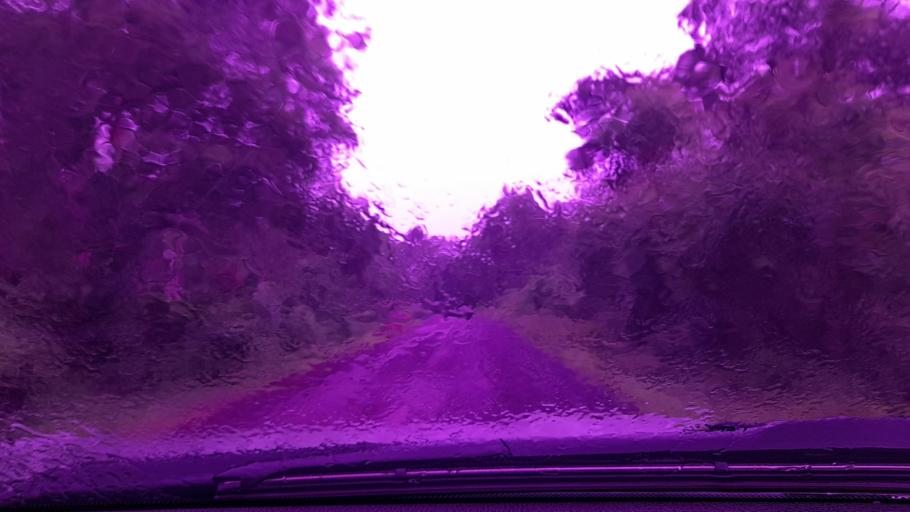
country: ET
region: Oromiya
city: Metu
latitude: 8.4616
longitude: 35.6392
